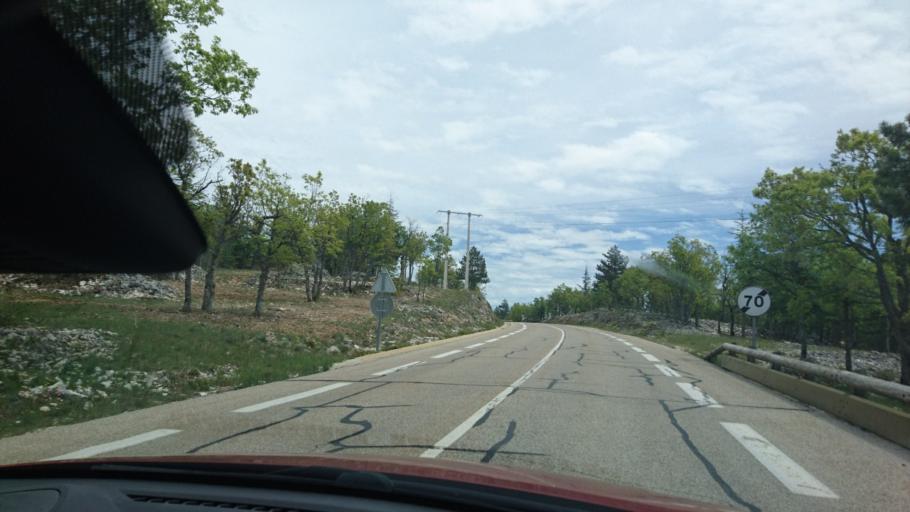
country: FR
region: Provence-Alpes-Cote d'Azur
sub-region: Departement du Vaucluse
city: Villes-sur-Auzon
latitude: 44.0907
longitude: 5.3064
